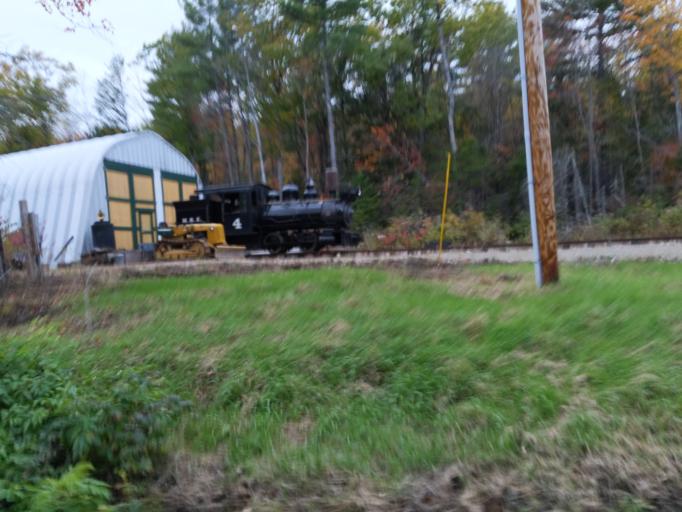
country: US
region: Maine
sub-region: Lincoln County
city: Wiscasset
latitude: 44.0724
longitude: -69.6215
